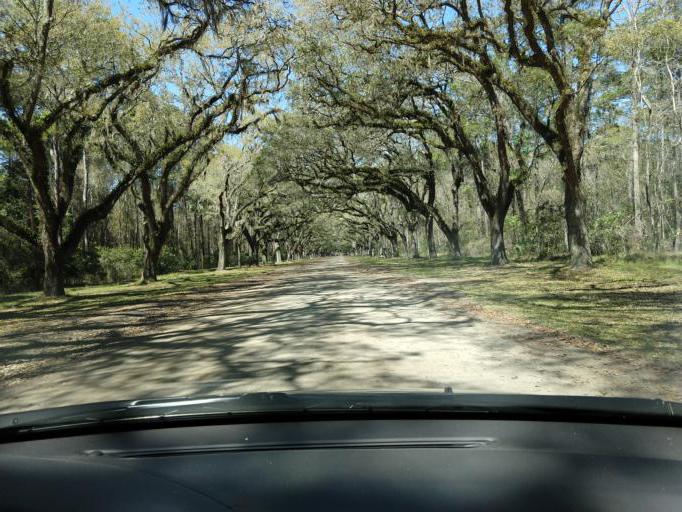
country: US
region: Georgia
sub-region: Chatham County
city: Isle of Hope
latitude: 31.9756
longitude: -81.0691
